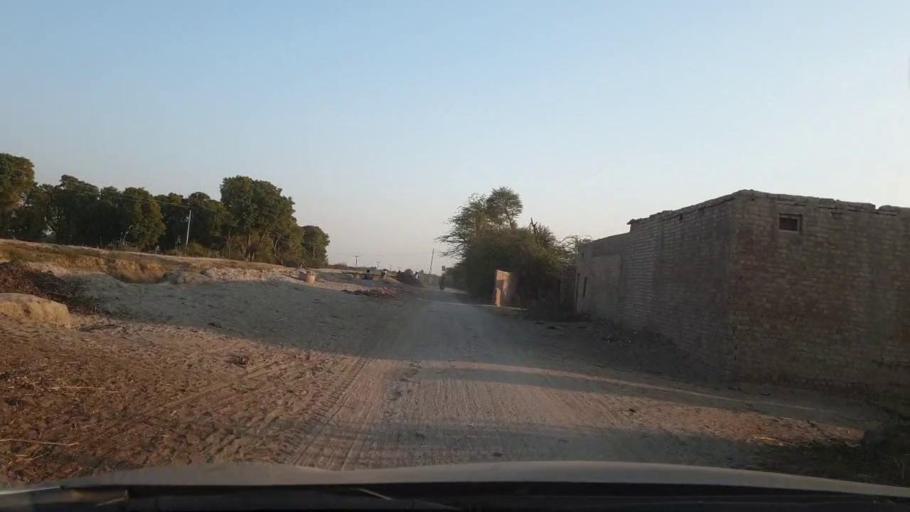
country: PK
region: Sindh
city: Tando Adam
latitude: 25.6843
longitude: 68.7452
